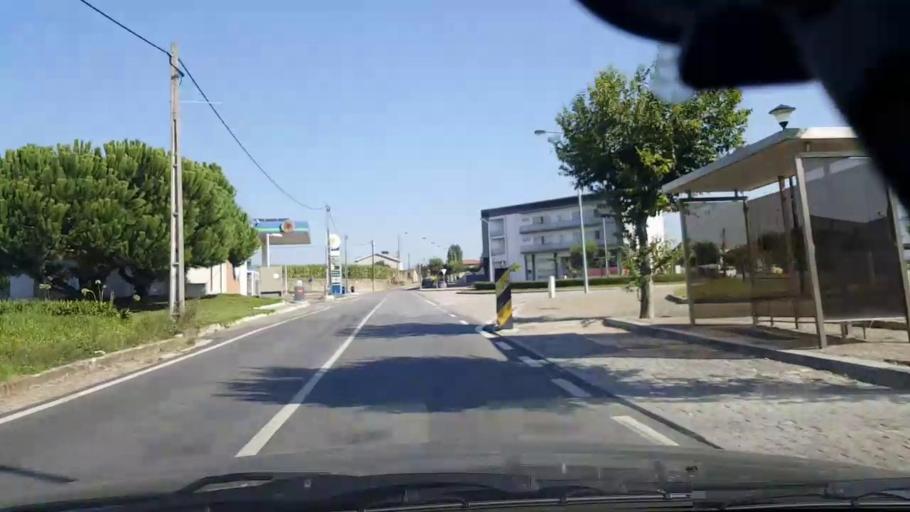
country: PT
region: Porto
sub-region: Maia
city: Gemunde
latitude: 41.3002
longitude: -8.6796
